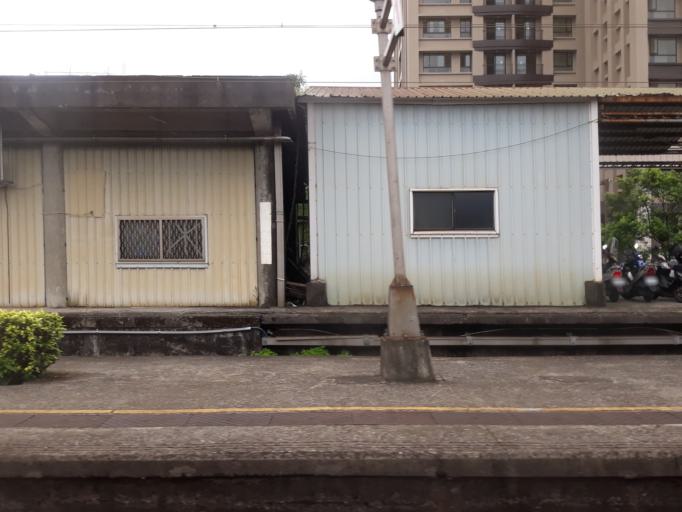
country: TW
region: Taiwan
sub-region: Yilan
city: Yilan
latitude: 24.6790
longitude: 121.7745
